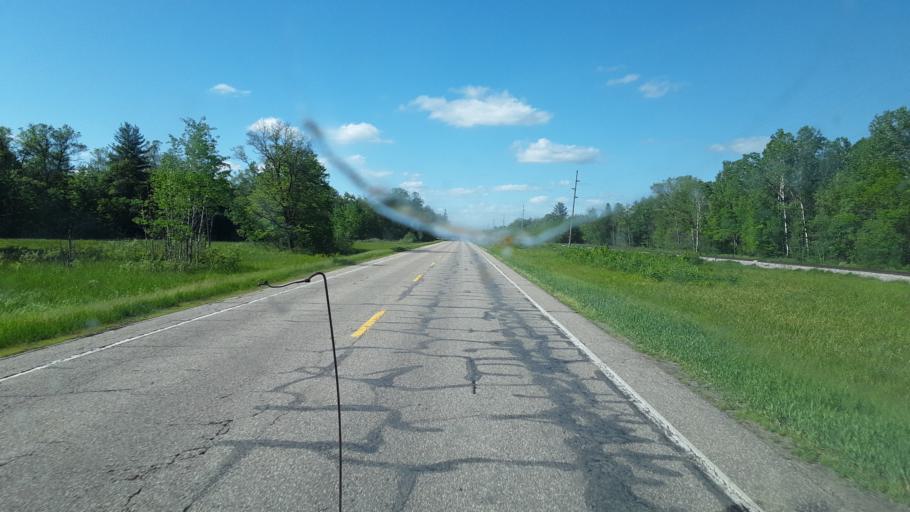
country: US
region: Wisconsin
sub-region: Wood County
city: Nekoosa
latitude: 44.2174
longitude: -90.1373
